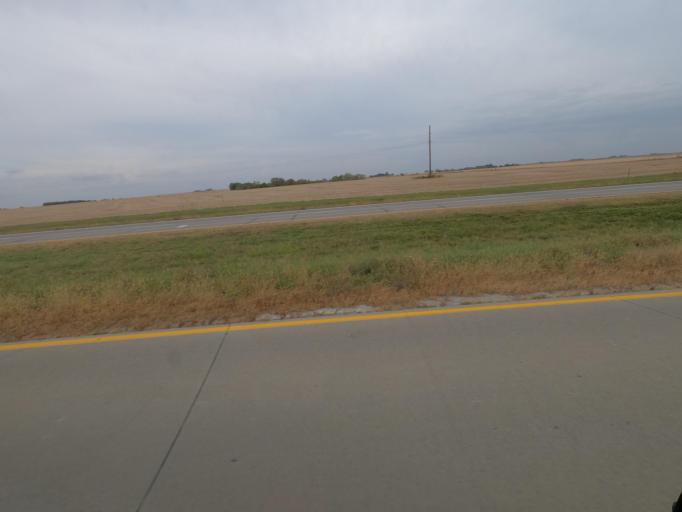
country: US
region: Iowa
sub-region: Marion County
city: Pella
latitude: 41.4334
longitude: -92.9928
